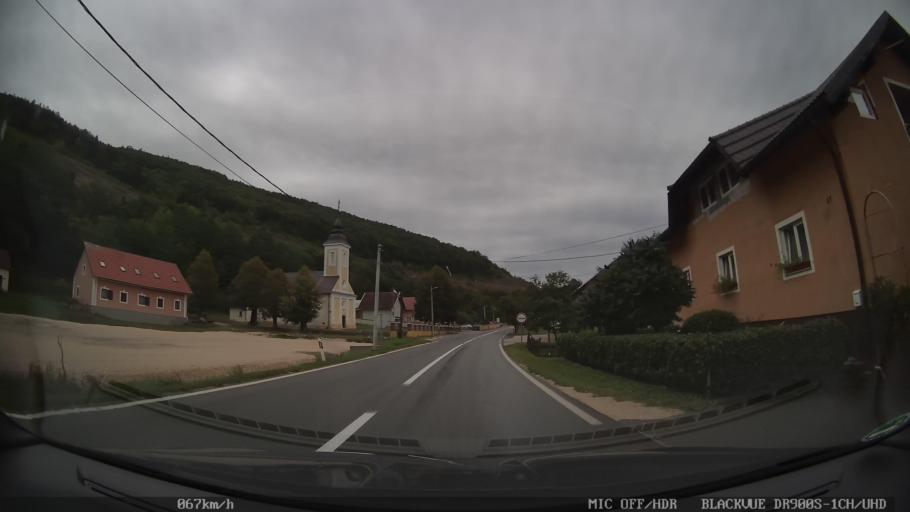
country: HR
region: Licko-Senjska
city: Otocac
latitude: 44.9007
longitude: 15.1806
